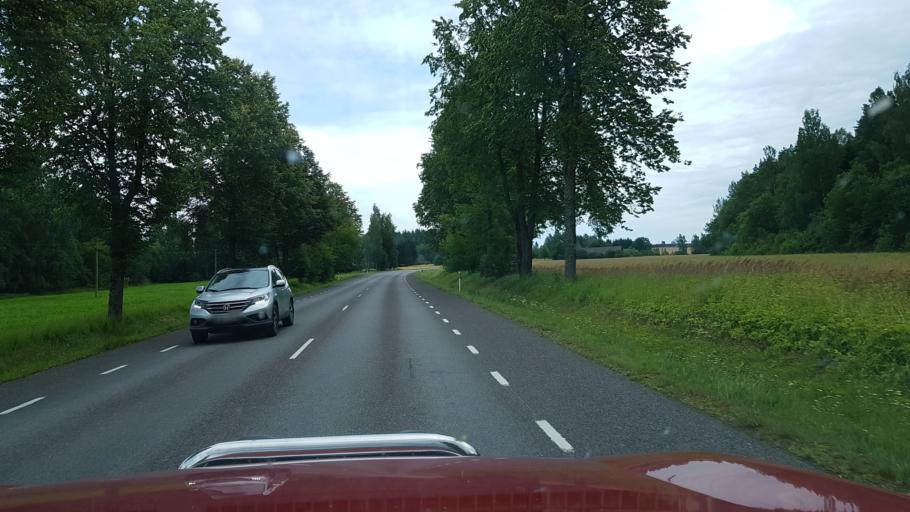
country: EE
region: Polvamaa
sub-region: Raepina vald
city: Rapina
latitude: 58.0968
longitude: 27.4088
